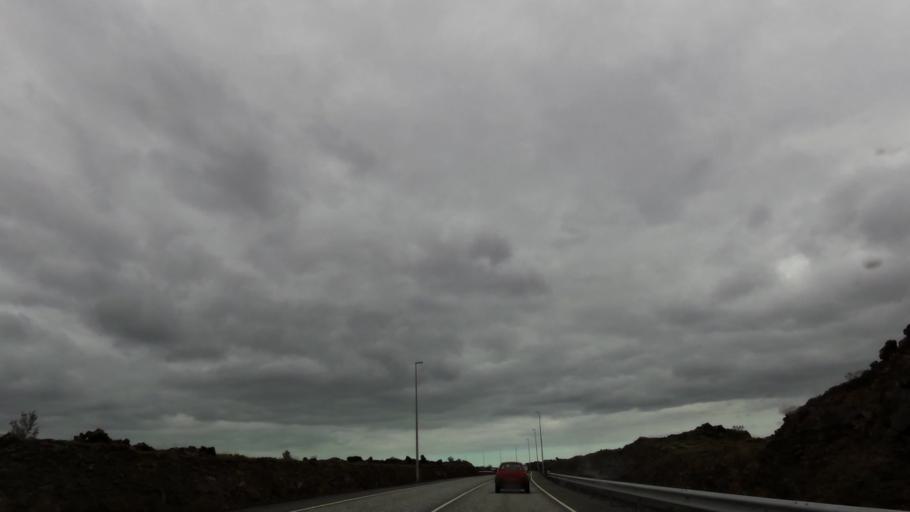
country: IS
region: Capital Region
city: Hafnarfjoerdur
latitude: 64.0872
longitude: -21.9598
